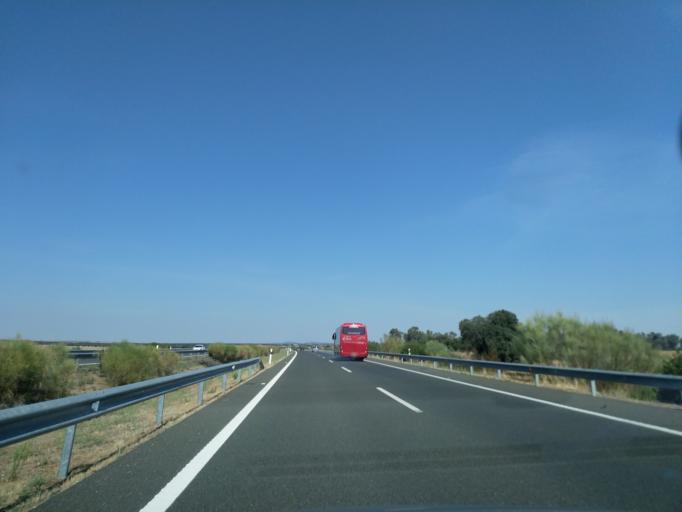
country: ES
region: Extremadura
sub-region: Provincia de Caceres
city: Casas de Don Antonio
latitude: 39.2466
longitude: -6.3062
